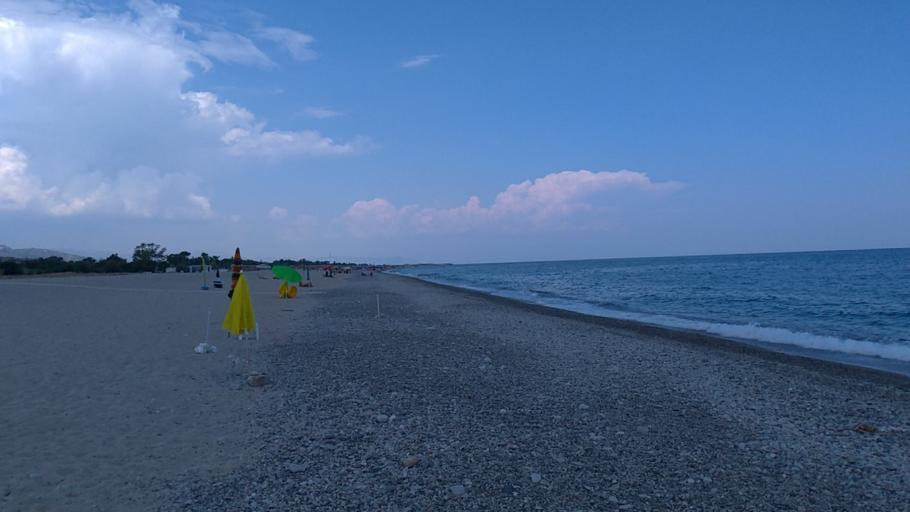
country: IT
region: Calabria
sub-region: Provincia di Catanzaro
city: Badolato Marina
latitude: 38.5749
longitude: 16.5705
